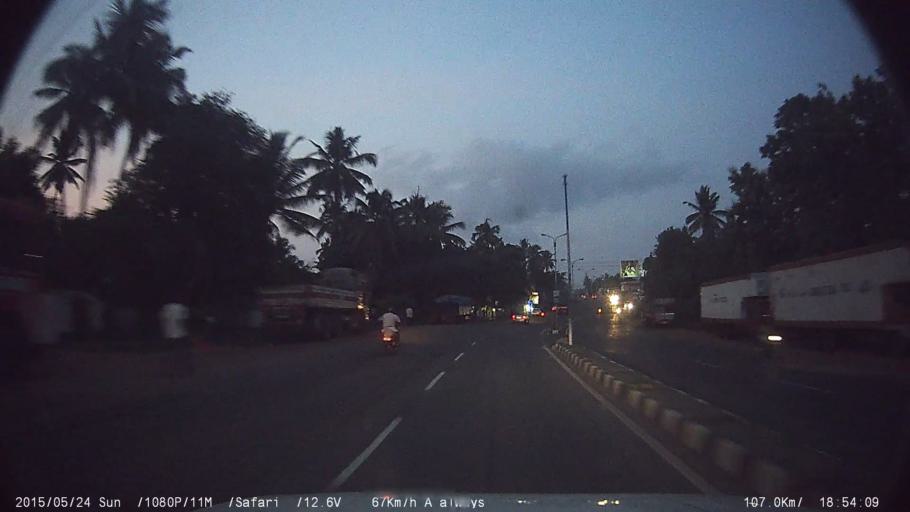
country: IN
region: Kerala
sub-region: Ernakulam
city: Angamali
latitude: 10.1689
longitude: 76.3718
